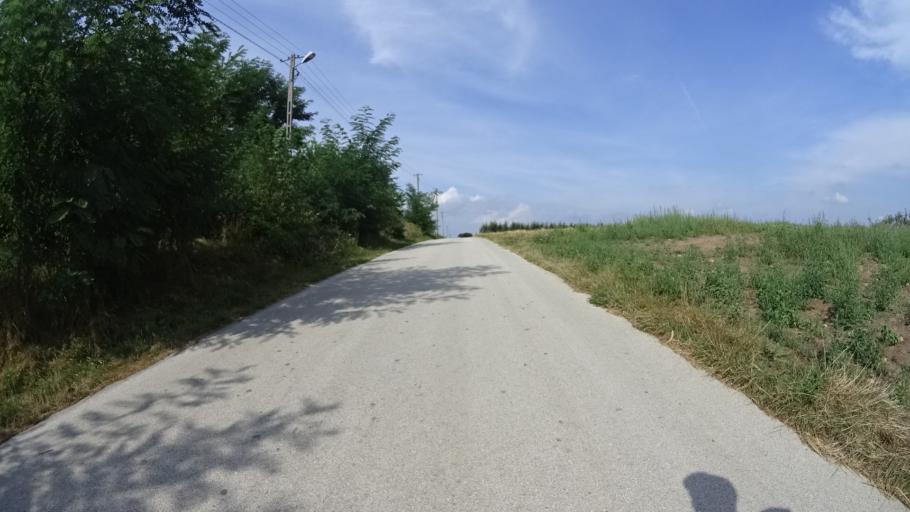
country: PL
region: Masovian Voivodeship
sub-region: Powiat grojecki
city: Goszczyn
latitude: 51.6852
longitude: 20.8424
